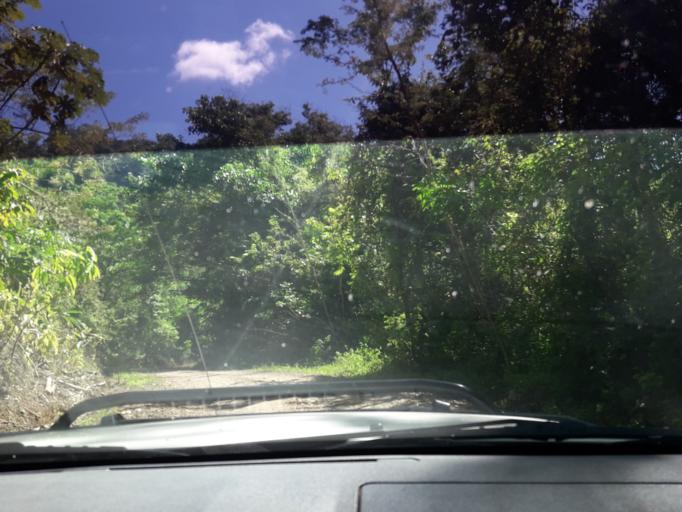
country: CR
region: Guanacaste
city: La Cruz
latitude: 11.2020
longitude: -85.6552
